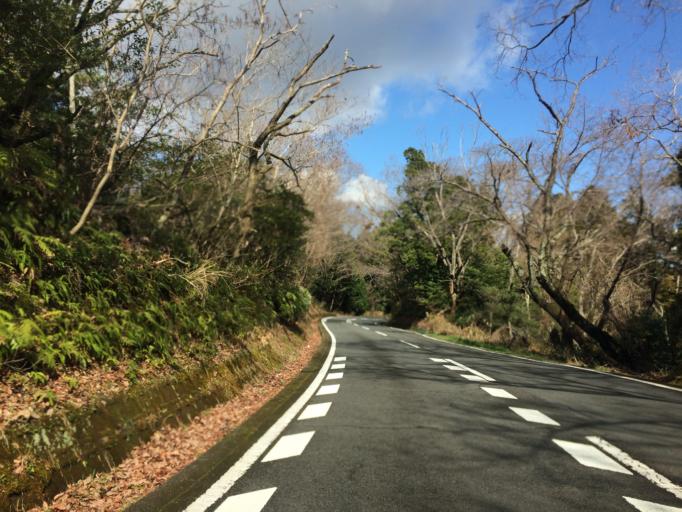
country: JP
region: Shizuoka
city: Shizuoka-shi
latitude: 34.9725
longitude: 138.4485
